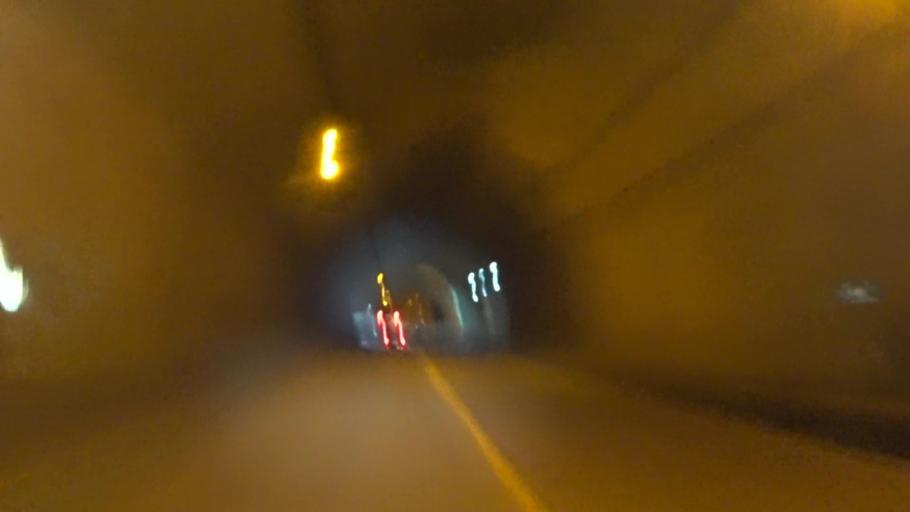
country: JP
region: Kyoto
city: Fukuchiyama
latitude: 35.4035
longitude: 135.0382
